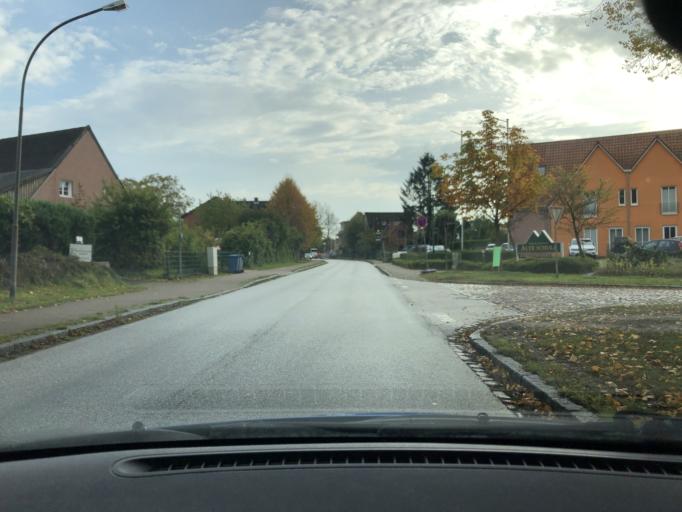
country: DE
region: Schleswig-Holstein
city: Siek
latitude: 53.6329
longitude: 10.2977
